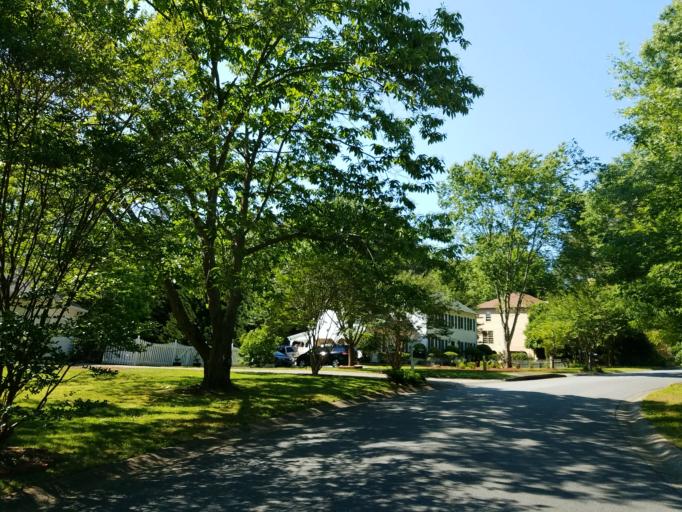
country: US
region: Georgia
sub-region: Cherokee County
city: Woodstock
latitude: 34.0304
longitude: -84.4998
